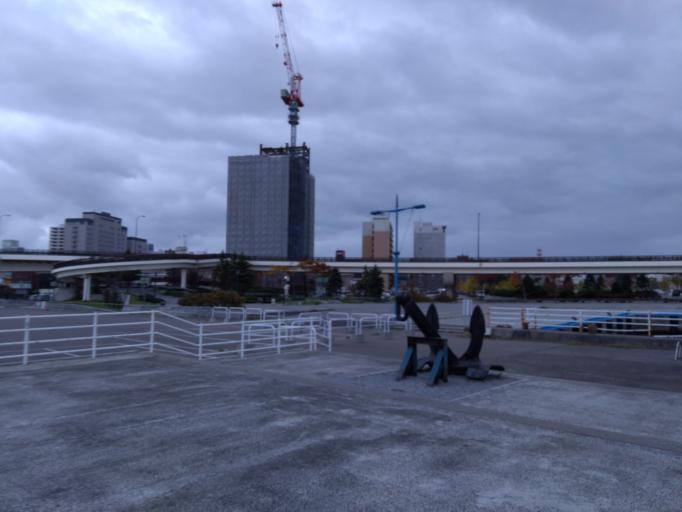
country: JP
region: Hokkaido
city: Hakodate
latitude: 41.7725
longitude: 140.7220
